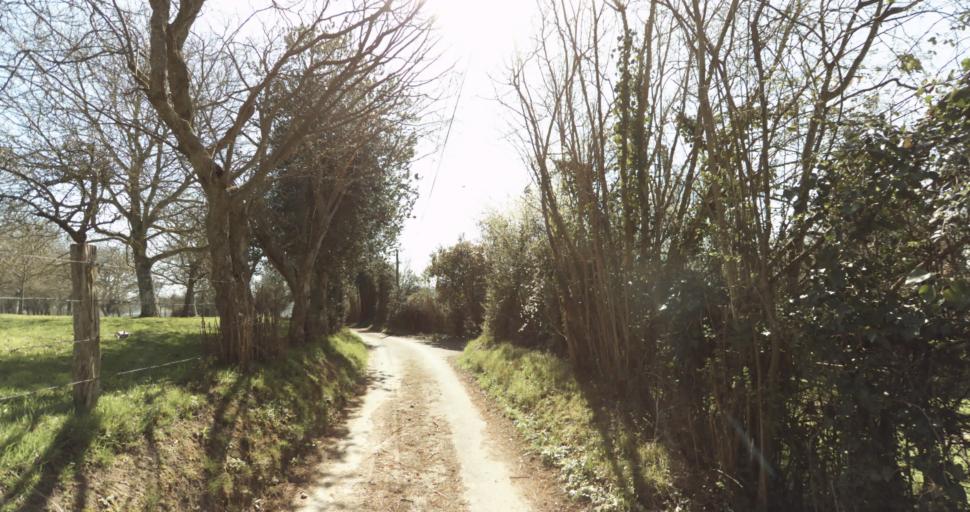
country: FR
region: Lower Normandy
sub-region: Departement du Calvados
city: Livarot
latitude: 49.0157
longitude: 0.0829
